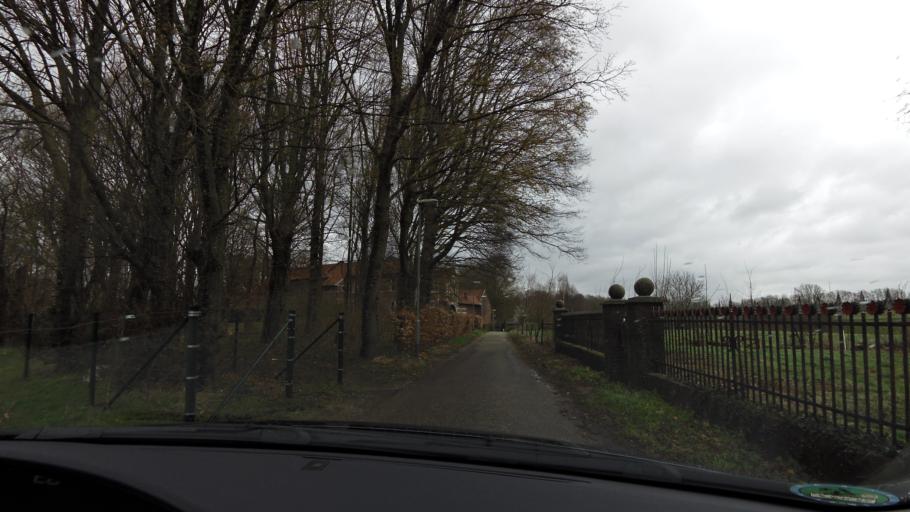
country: NL
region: Limburg
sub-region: Gemeente Beek
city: Beek
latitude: 50.9208
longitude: 5.8010
